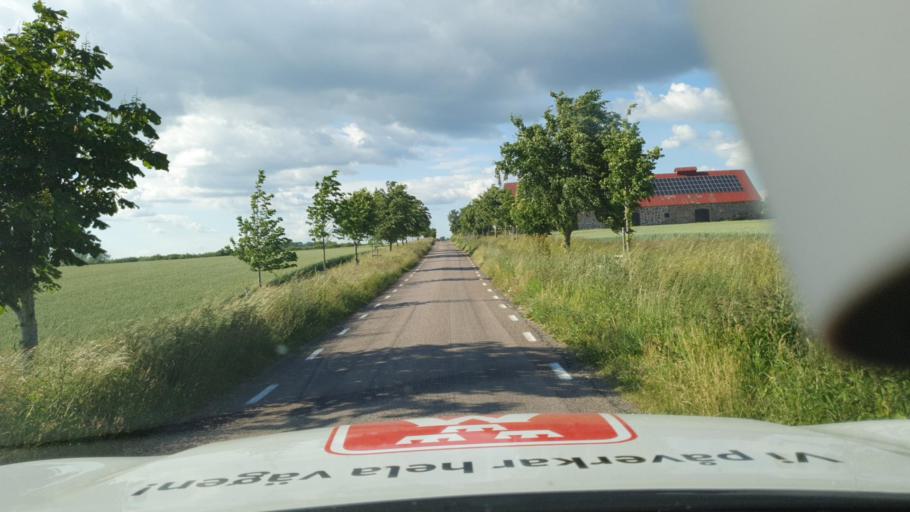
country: SE
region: Skane
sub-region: Ystads Kommun
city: Ystad
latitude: 55.4317
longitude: 13.7381
